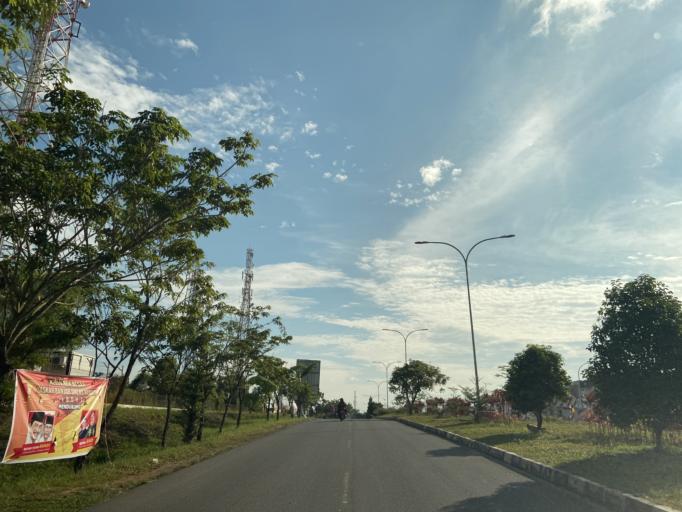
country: SG
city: Singapore
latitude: 1.1061
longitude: 104.0780
